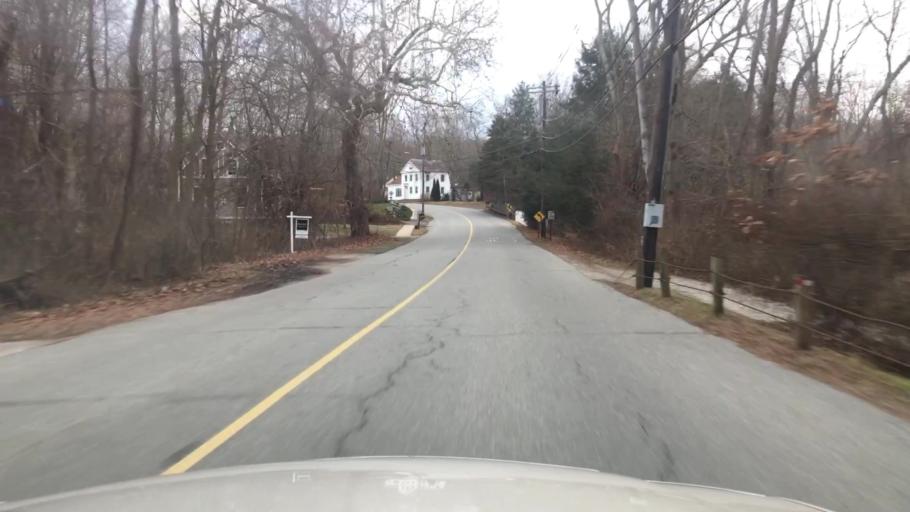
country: US
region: Connecticut
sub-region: Middlesex County
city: Essex Village
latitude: 41.3633
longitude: -72.4010
